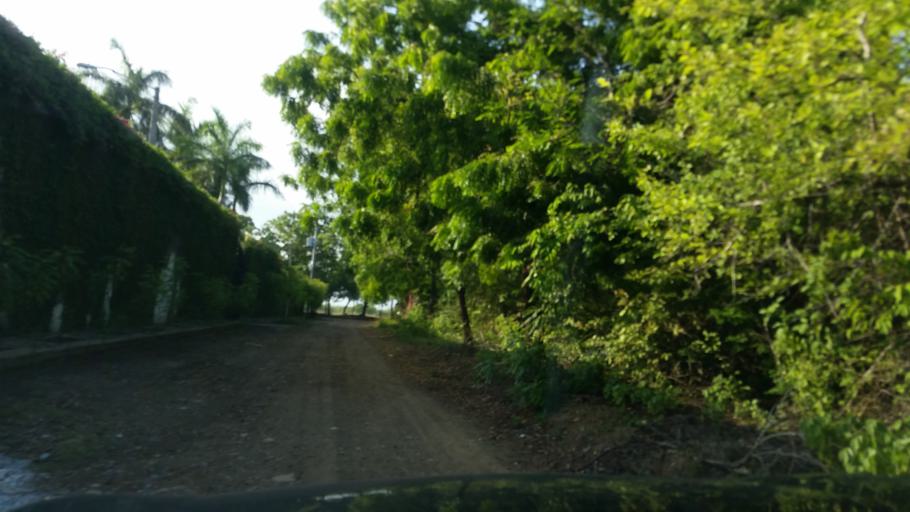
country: NI
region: Managua
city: Masachapa
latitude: 11.7593
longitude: -86.4911
